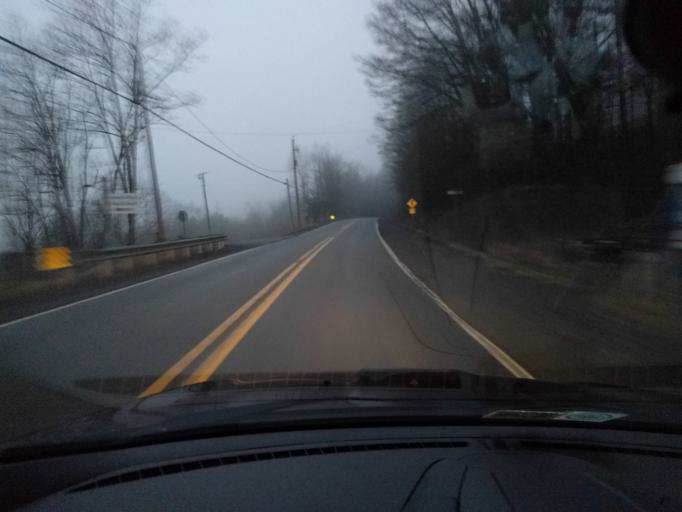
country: US
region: West Virginia
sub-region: Greenbrier County
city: Rainelle
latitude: 37.9717
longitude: -80.8143
